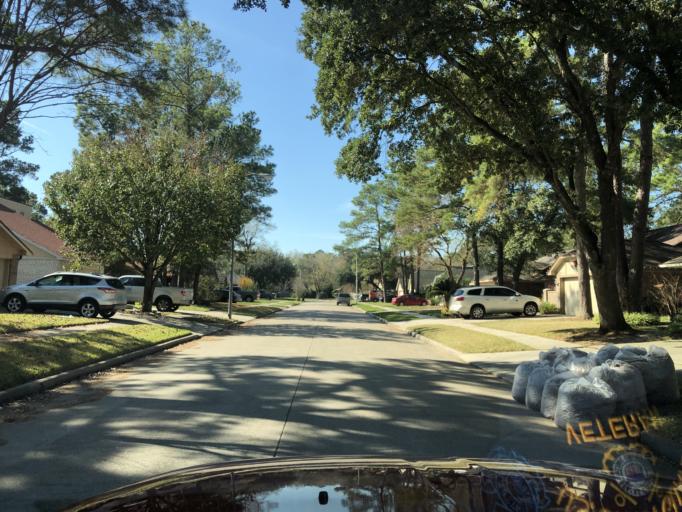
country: US
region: Texas
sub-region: Harris County
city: Tomball
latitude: 30.0203
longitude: -95.5575
